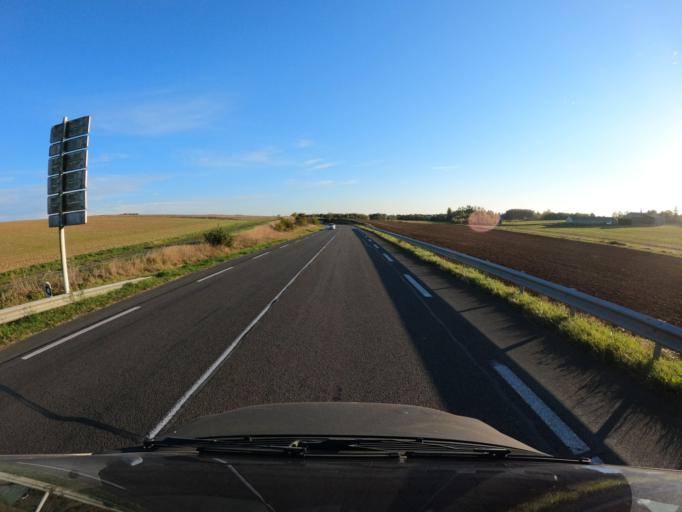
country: FR
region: Pays de la Loire
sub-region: Departement de la Vendee
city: Sainte-Hermine
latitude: 46.5624
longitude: -1.0468
